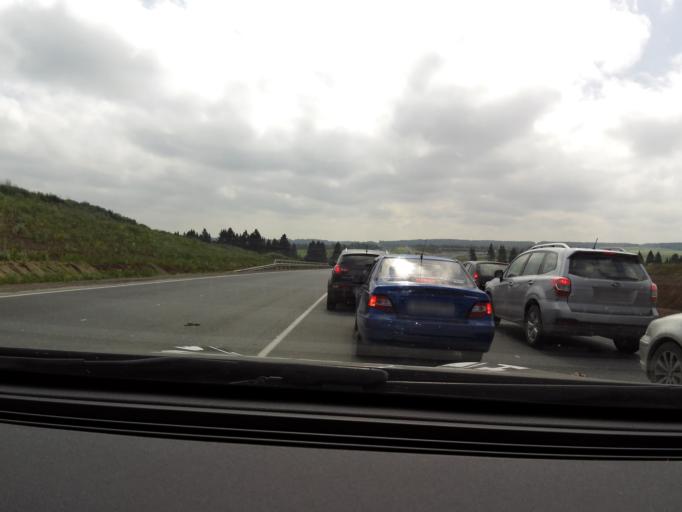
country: RU
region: Perm
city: Zvezdnyy
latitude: 57.7890
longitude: 56.3385
